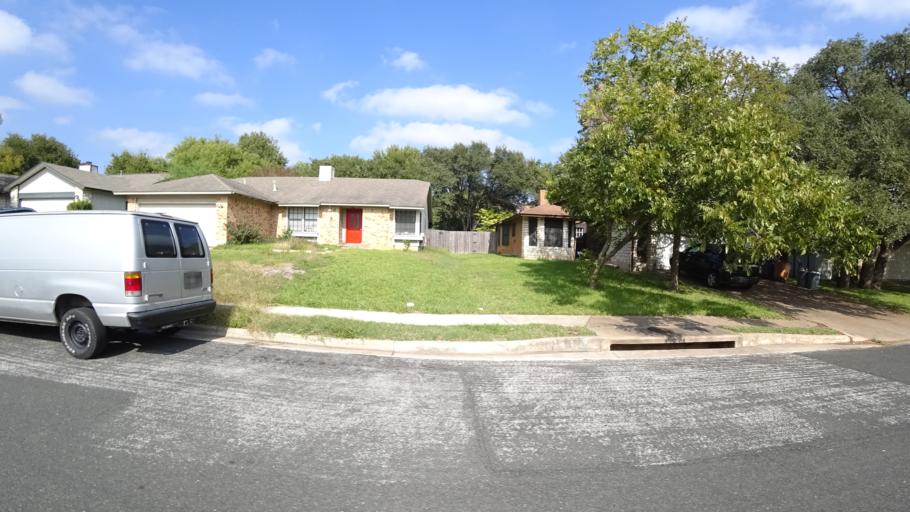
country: US
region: Texas
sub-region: Travis County
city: Shady Hollow
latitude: 30.1999
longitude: -97.8228
